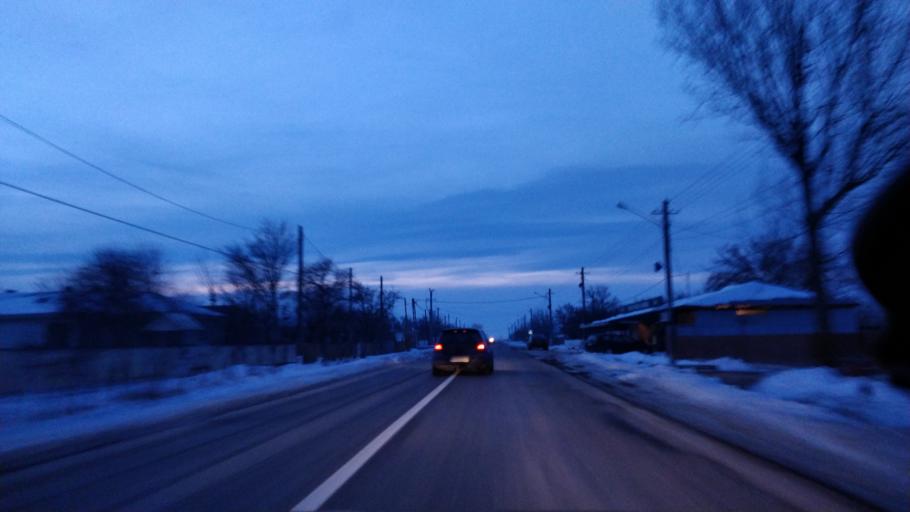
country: RO
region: Galati
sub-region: Comuna Liesti
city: Liesti
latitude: 45.5891
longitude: 27.4893
